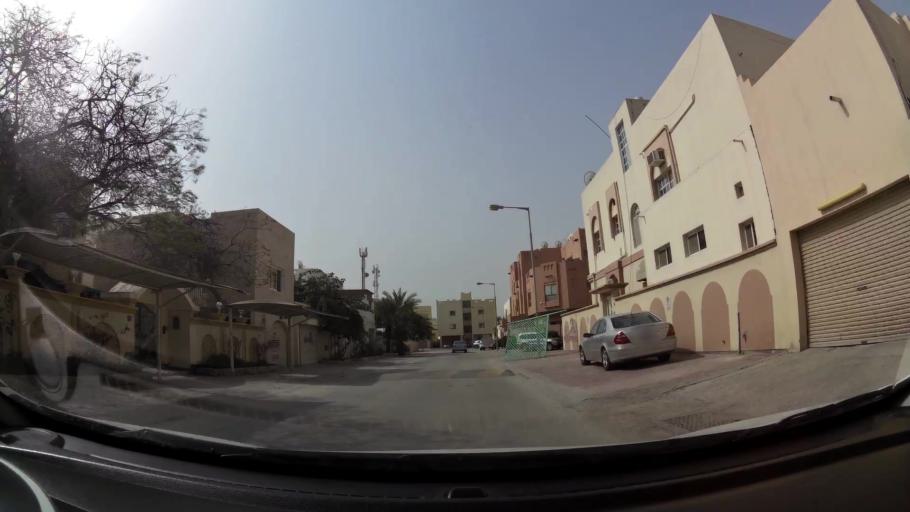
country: BH
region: Manama
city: Jidd Hafs
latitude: 26.2338
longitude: 50.5261
